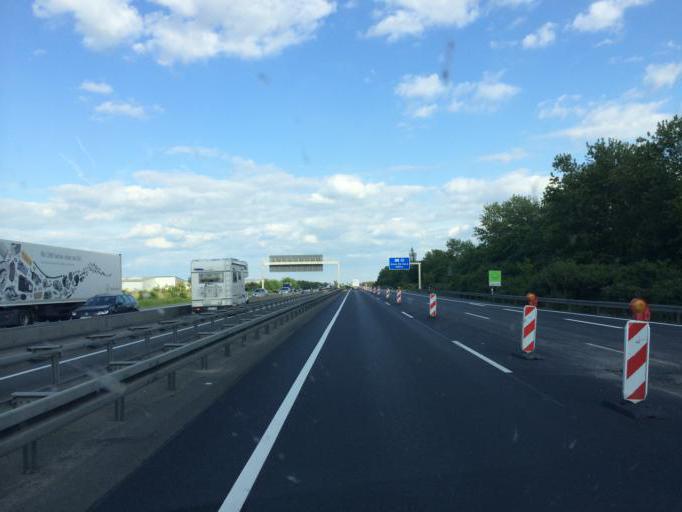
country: DE
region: Lower Saxony
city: Klein Schwulper
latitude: 52.3238
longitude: 10.4775
